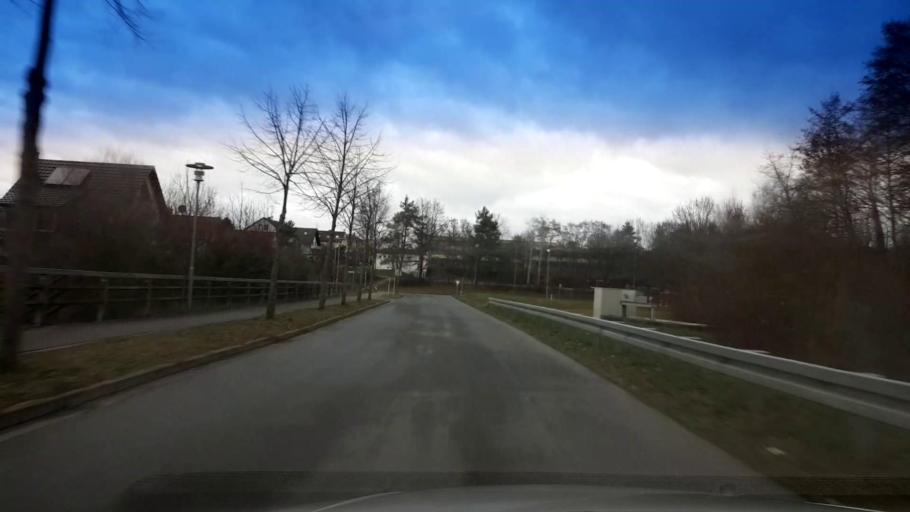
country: DE
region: Bavaria
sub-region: Upper Franconia
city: Breitengussbach
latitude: 49.9698
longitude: 10.8948
